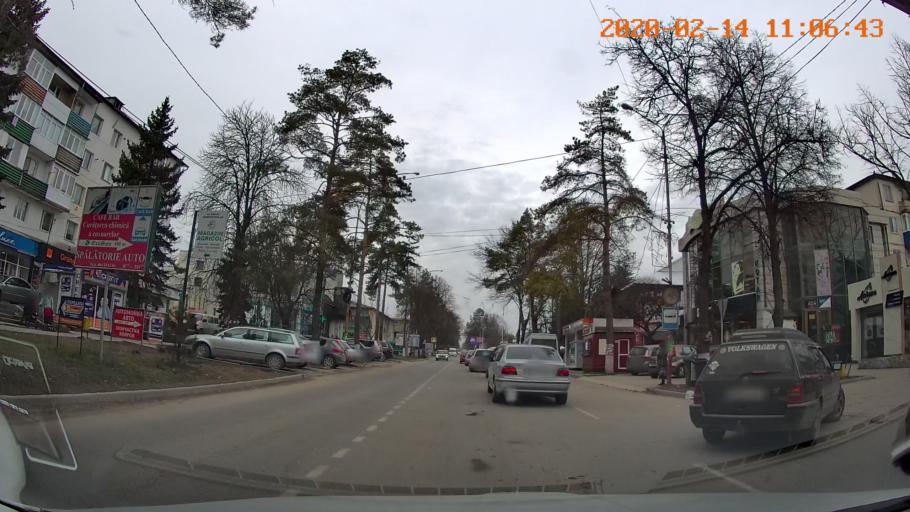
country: MD
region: Raionul Edinet
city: Edinet
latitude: 48.1686
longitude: 27.3072
